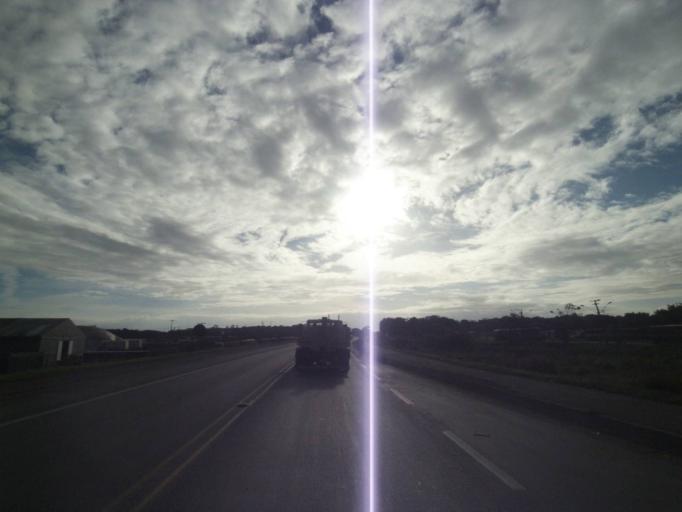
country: BR
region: Parana
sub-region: Paranagua
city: Paranagua
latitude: -25.5362
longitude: -48.5561
